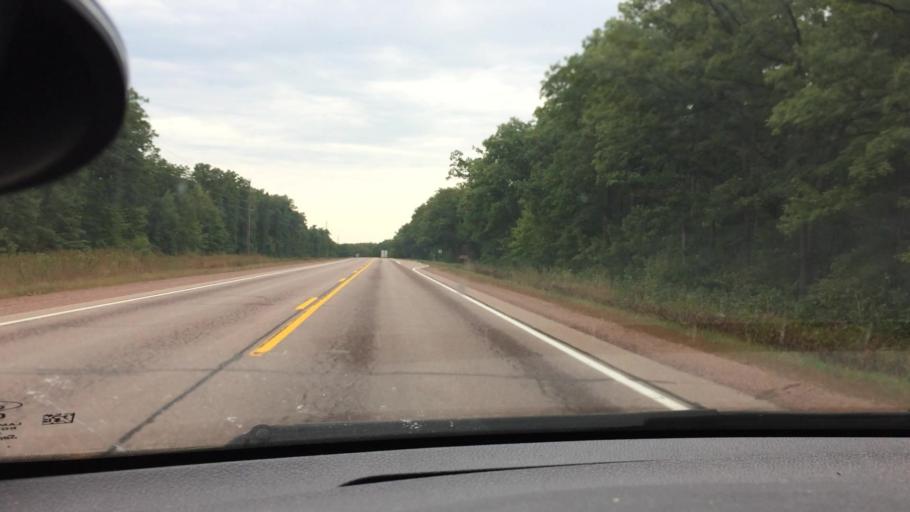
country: US
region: Wisconsin
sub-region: Clark County
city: Neillsville
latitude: 44.5799
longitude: -90.7399
